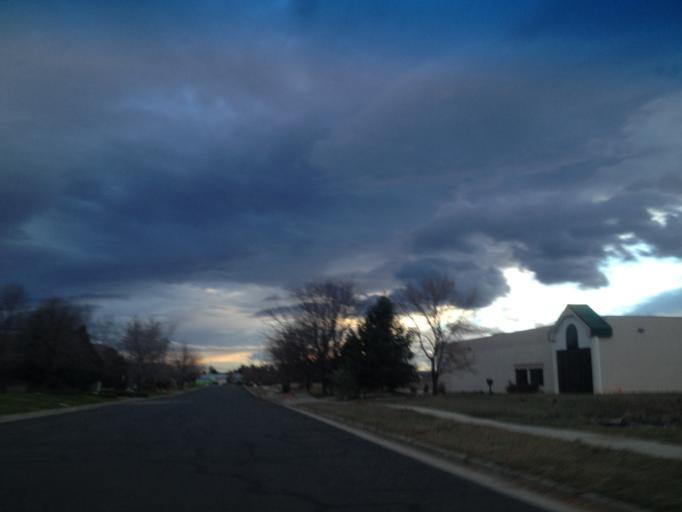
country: US
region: Colorado
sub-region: Boulder County
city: Louisville
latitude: 39.9626
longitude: -105.1238
